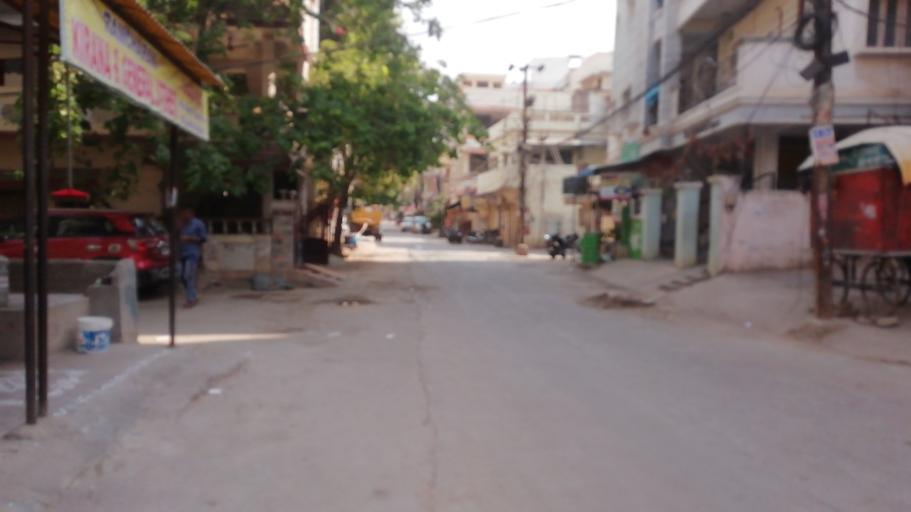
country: IN
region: Telangana
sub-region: Rangareddi
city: Gaddi Annaram
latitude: 17.3663
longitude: 78.5330
